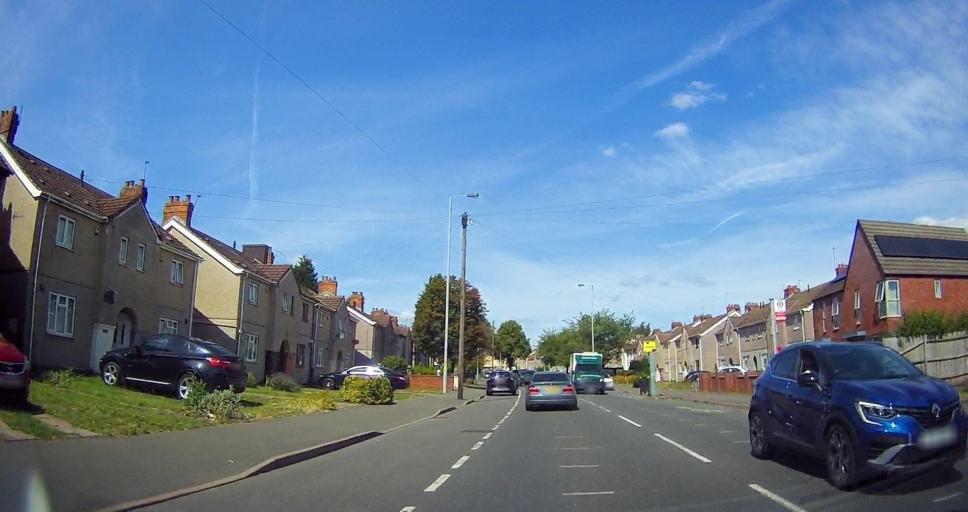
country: GB
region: England
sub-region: Wolverhampton
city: Wolverhampton
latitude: 52.5698
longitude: -2.1181
